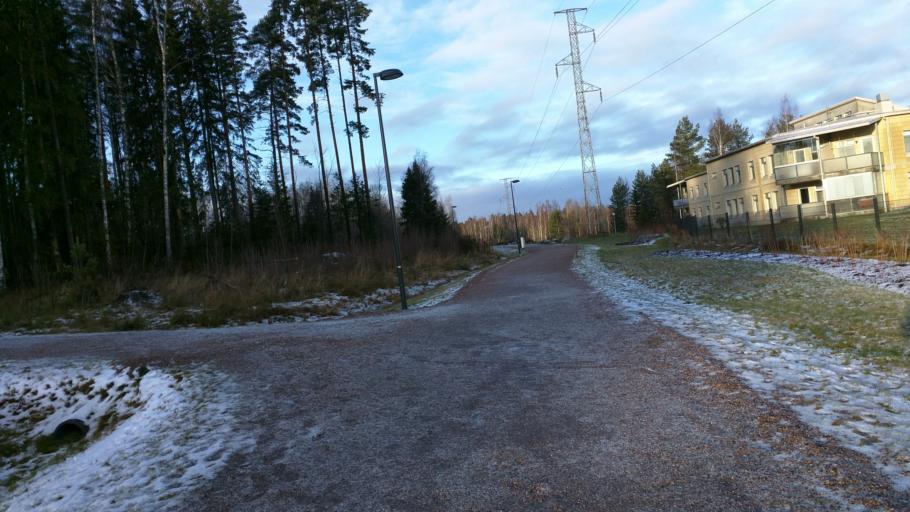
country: FI
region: Uusimaa
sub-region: Helsinki
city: Kilo
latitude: 60.2567
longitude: 24.7971
